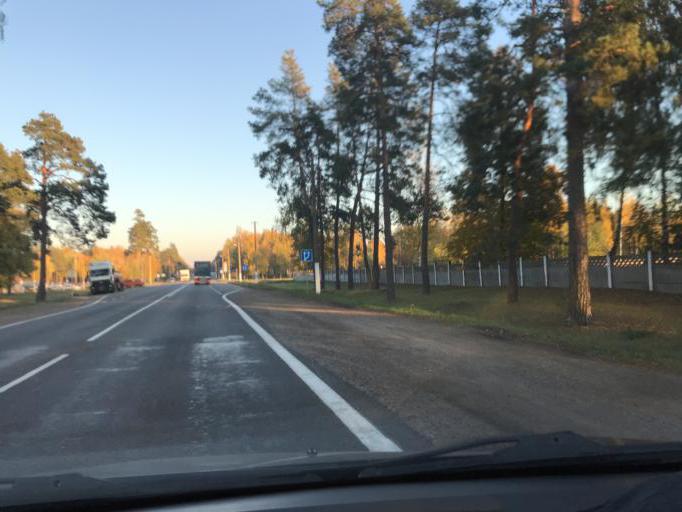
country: BY
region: Minsk
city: Staryya Darohi
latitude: 53.0343
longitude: 28.2389
